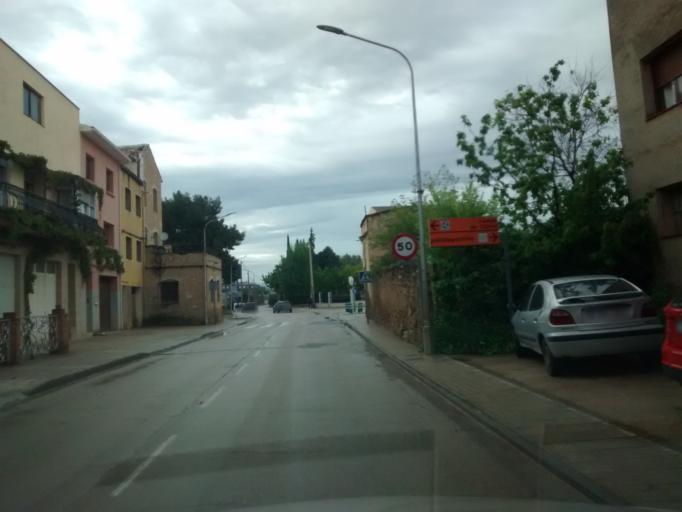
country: ES
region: Aragon
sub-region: Provincia de Zaragoza
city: Maella
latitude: 41.1237
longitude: 0.1364
